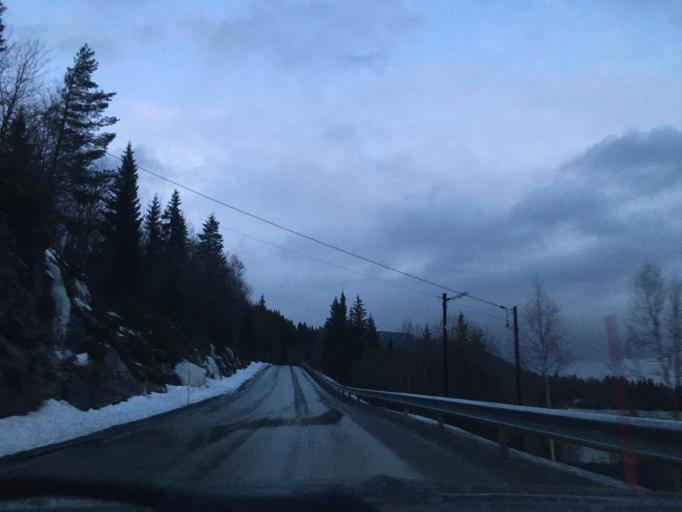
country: NO
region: Nordland
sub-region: Rana
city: Hauknes
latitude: 66.3042
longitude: 13.9539
